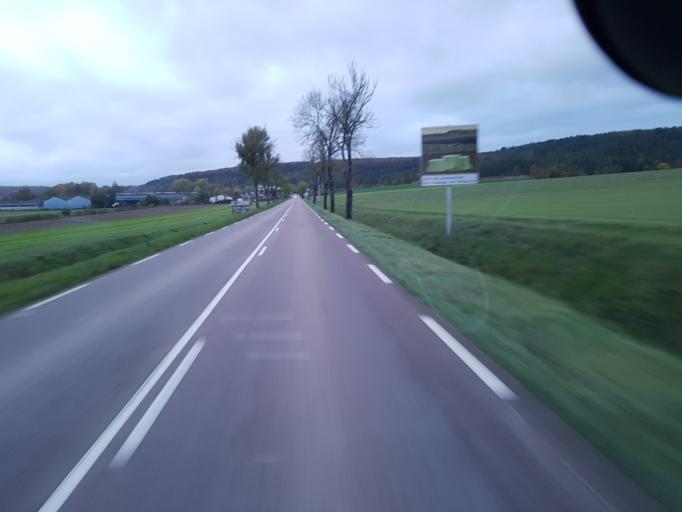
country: FR
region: Champagne-Ardenne
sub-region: Departement de l'Aube
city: Mussy-sur-Seine
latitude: 47.9877
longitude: 4.4848
